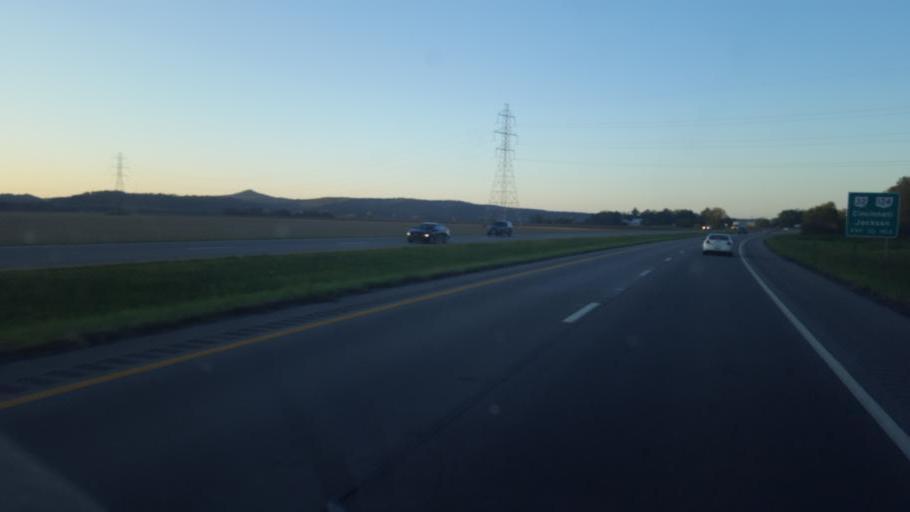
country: US
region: Ohio
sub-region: Pike County
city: Piketon
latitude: 39.0357
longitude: -83.0280
